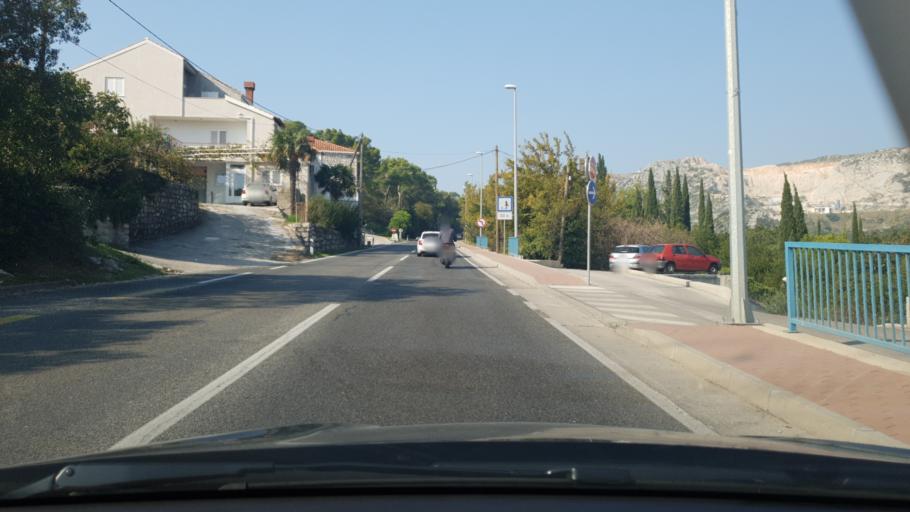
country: HR
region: Dubrovacko-Neretvanska
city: Cibaca
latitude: 42.6275
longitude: 18.1688
